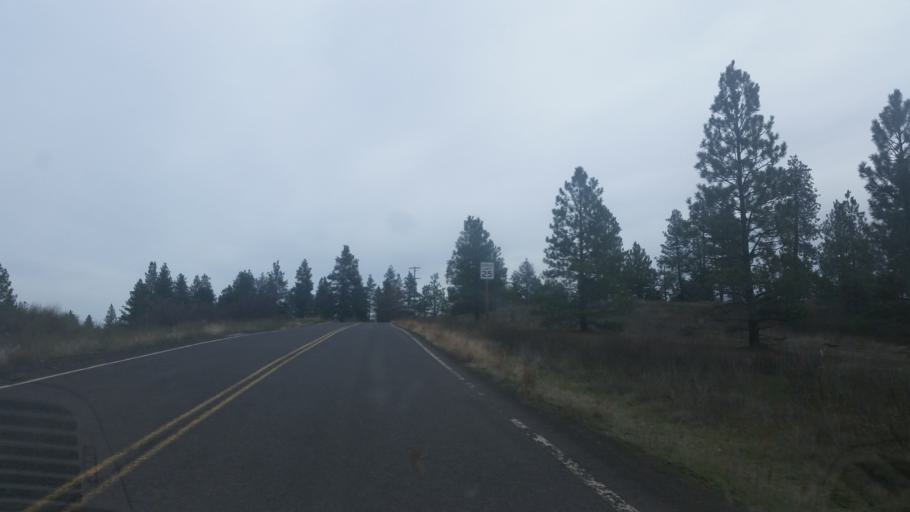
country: US
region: Washington
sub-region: Spokane County
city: Cheney
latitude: 47.2281
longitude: -117.4838
